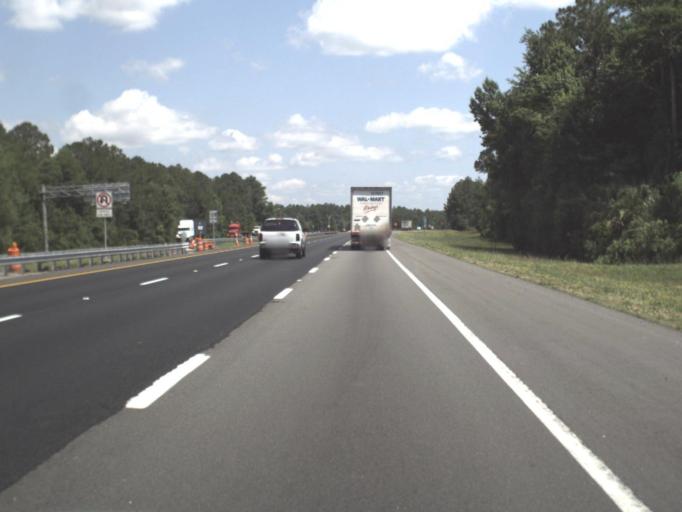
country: US
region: Florida
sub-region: Nassau County
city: Yulee
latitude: 30.6910
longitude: -81.6750
